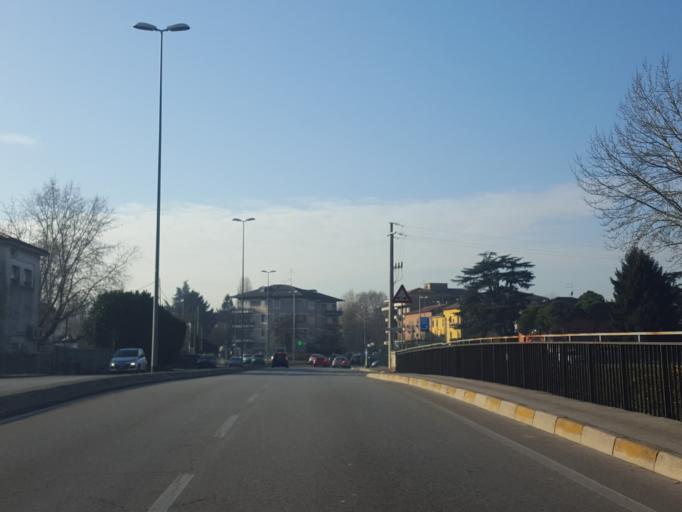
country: IT
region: Veneto
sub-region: Provincia di Vicenza
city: Vicenza
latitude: 45.5590
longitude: 11.5239
